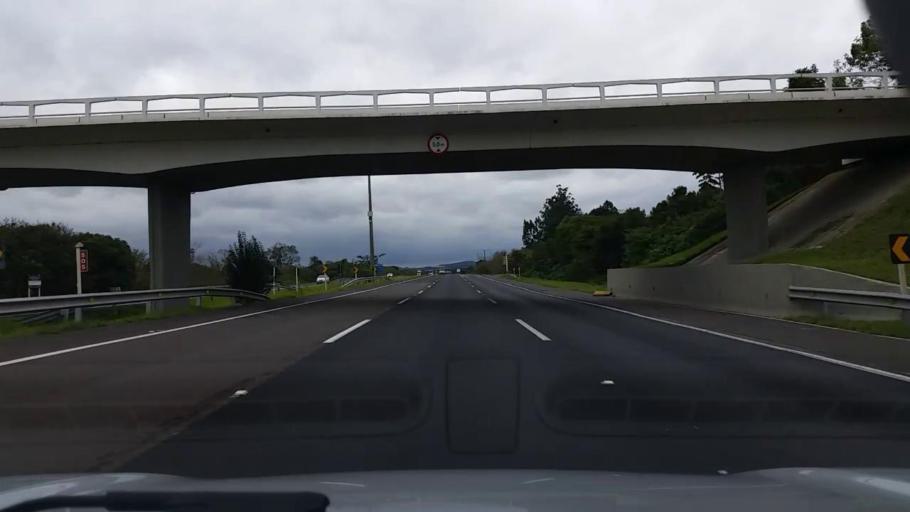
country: BR
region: Rio Grande do Sul
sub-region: Osorio
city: Osorio
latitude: -29.8755
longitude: -50.4253
